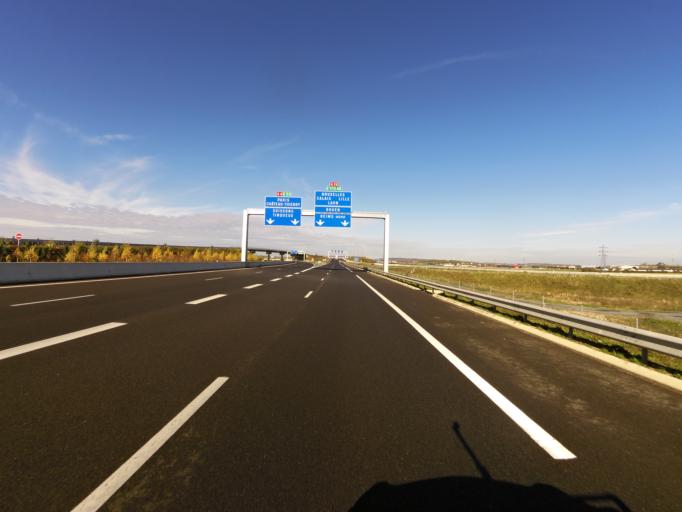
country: FR
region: Champagne-Ardenne
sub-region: Departement de la Marne
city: Tinqueux
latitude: 49.2413
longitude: 3.9673
